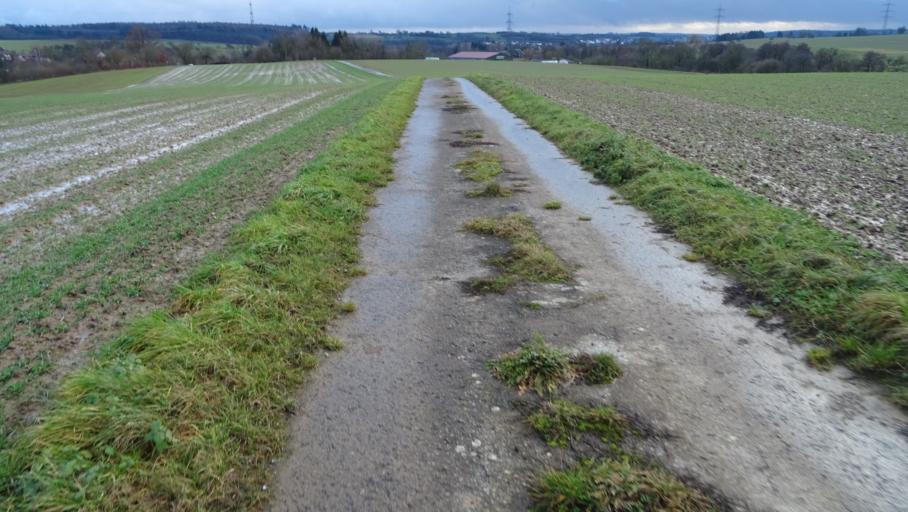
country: DE
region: Baden-Wuerttemberg
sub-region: Karlsruhe Region
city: Seckach
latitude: 49.4344
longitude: 9.2868
